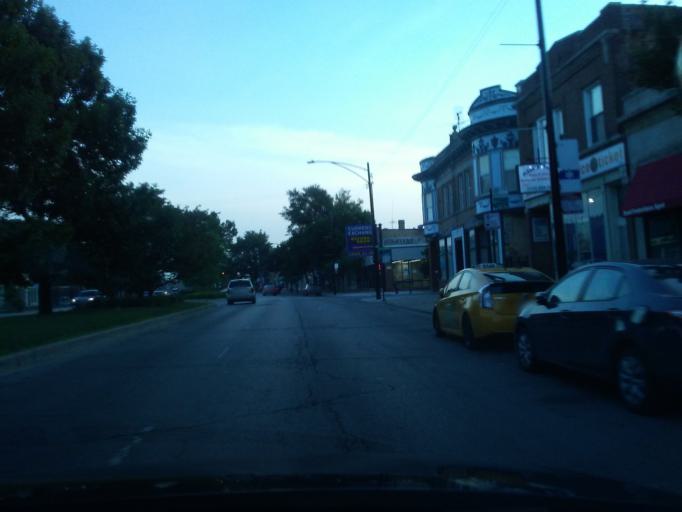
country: US
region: Illinois
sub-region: Cook County
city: Evanston
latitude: 41.9960
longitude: -87.6701
